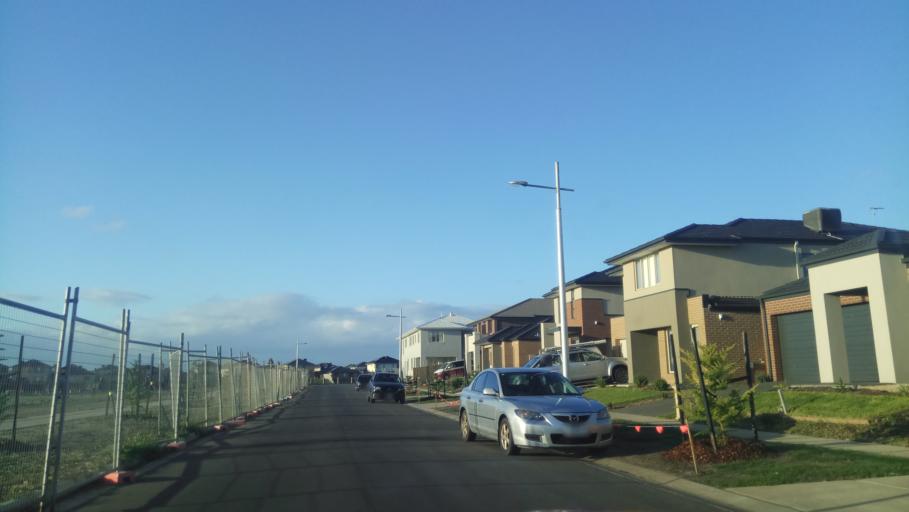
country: AU
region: Victoria
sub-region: Hobsons Bay
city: Altona Meadows
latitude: -37.9069
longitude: 144.7764
